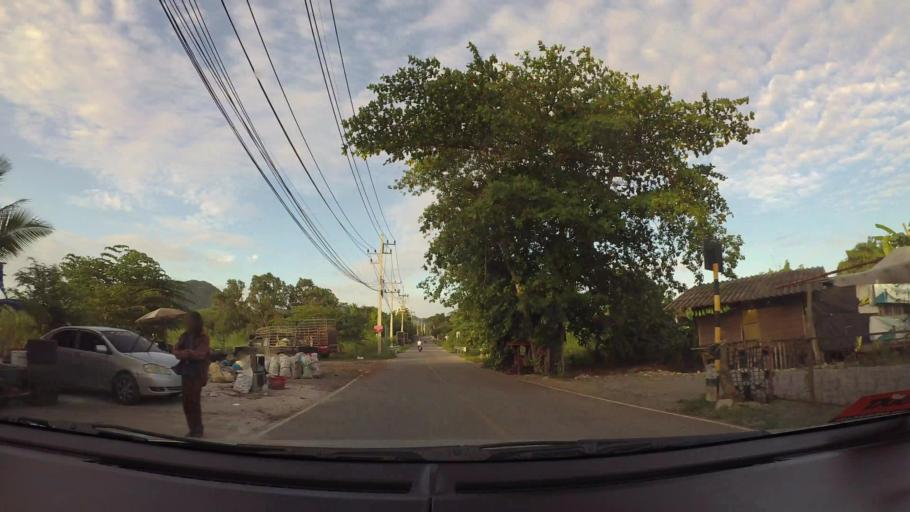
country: TH
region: Chon Buri
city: Sattahip
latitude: 12.7480
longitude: 100.9349
